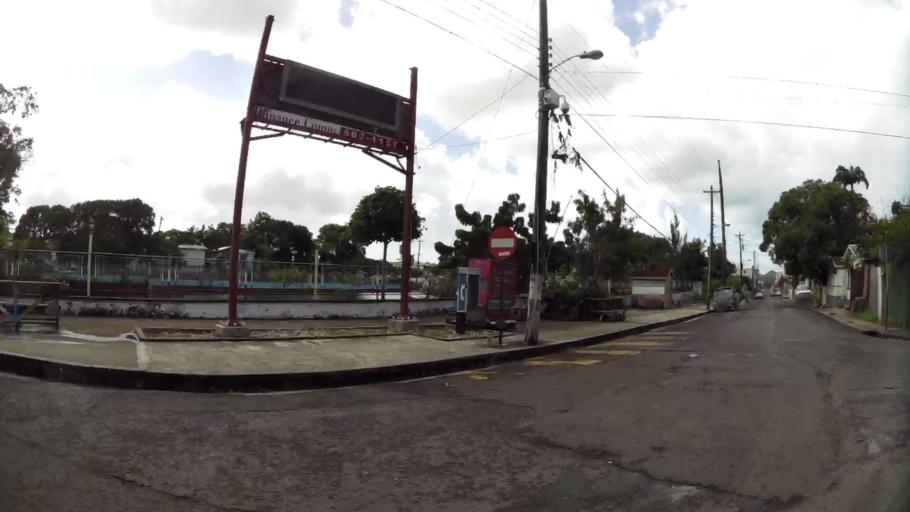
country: AG
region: Saint John
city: Saint John's
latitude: 17.1195
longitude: -61.8400
